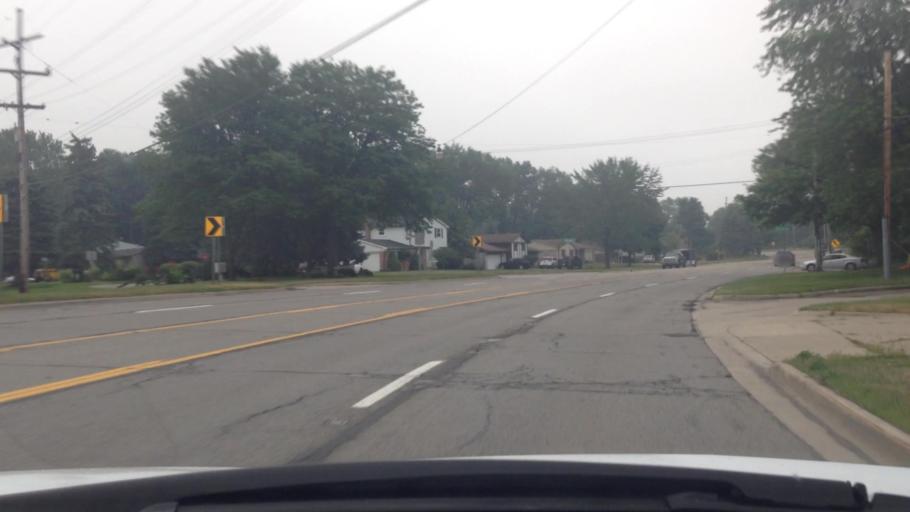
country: US
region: Michigan
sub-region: Oakland County
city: Waterford
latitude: 42.6865
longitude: -83.3452
